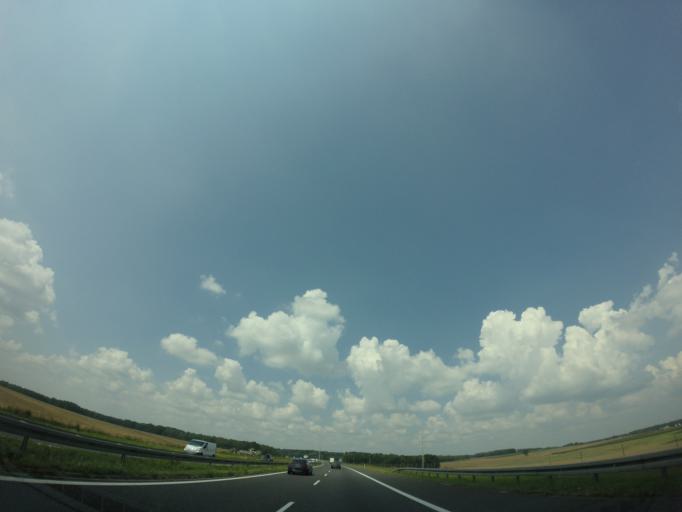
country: PL
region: Opole Voivodeship
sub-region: Powiat strzelecki
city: Ujazd
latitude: 50.4202
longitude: 18.3990
